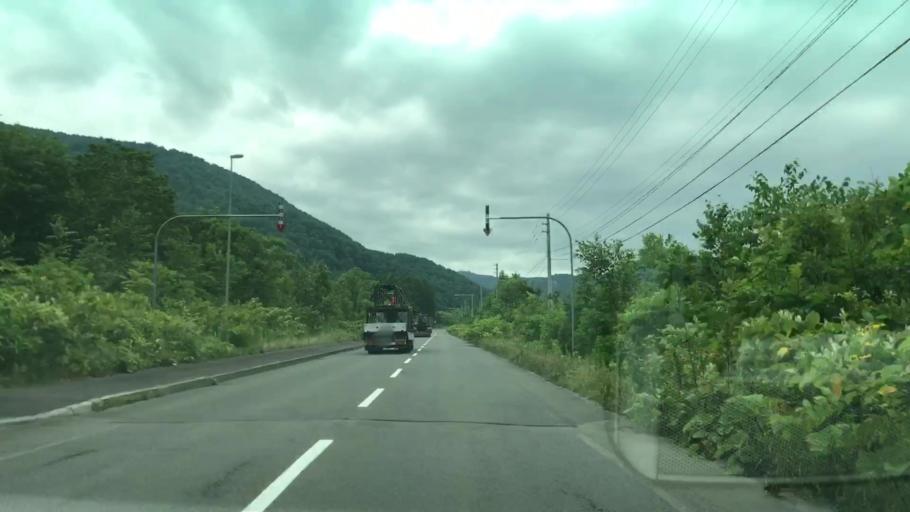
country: JP
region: Hokkaido
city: Yoichi
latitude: 43.0334
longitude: 140.8643
